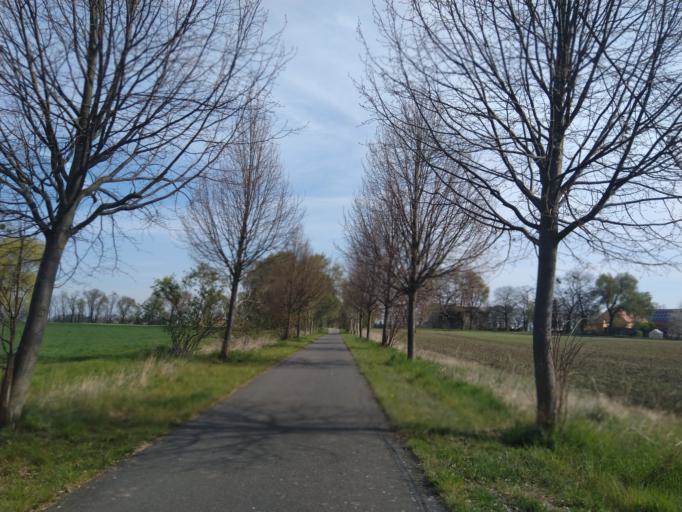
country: DE
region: Brandenburg
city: Wriezen
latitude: 52.7398
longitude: 14.1586
